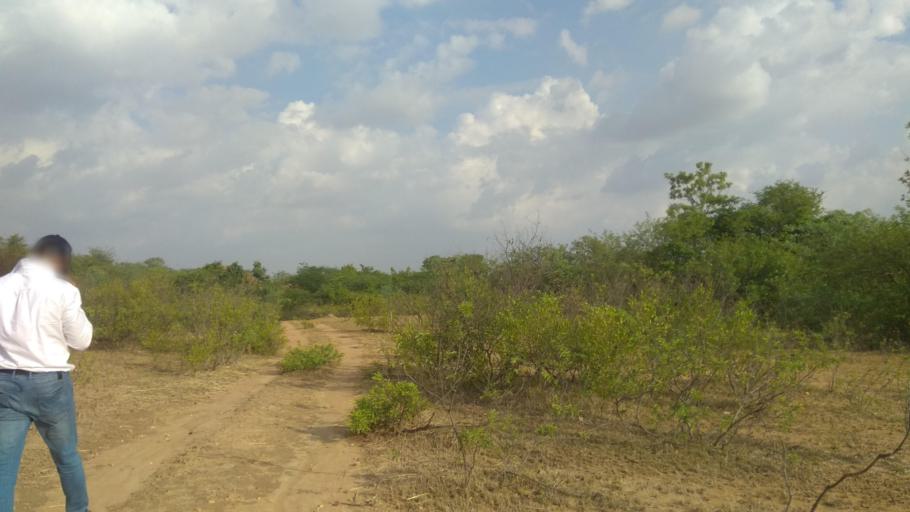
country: IN
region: Telangana
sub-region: Mahbubnagar
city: Farrukhnagar
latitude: 16.8867
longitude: 78.4791
